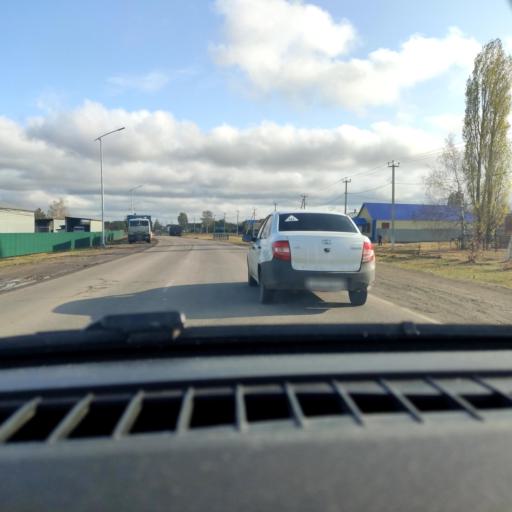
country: RU
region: Belgorod
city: Ilovka
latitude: 50.7310
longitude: 38.6908
